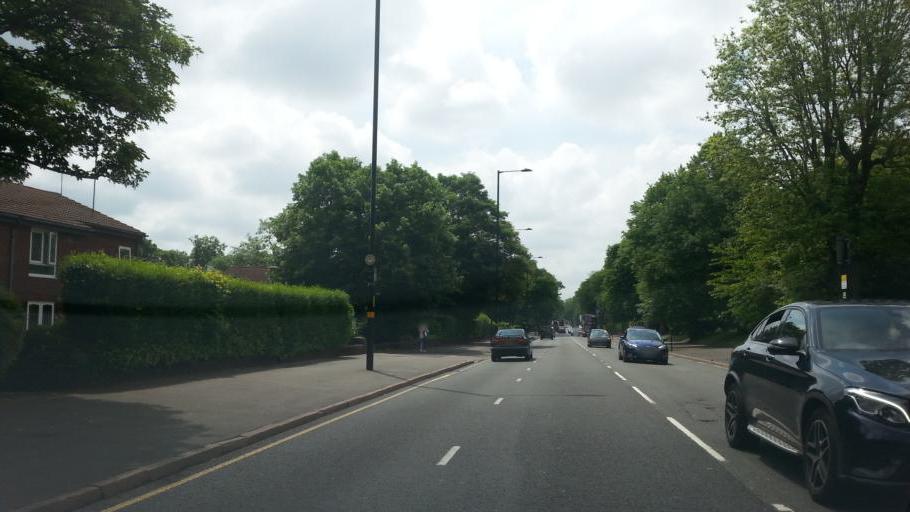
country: GB
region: England
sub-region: City and Borough of Birmingham
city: Birmingham
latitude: 52.4623
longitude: -1.9045
